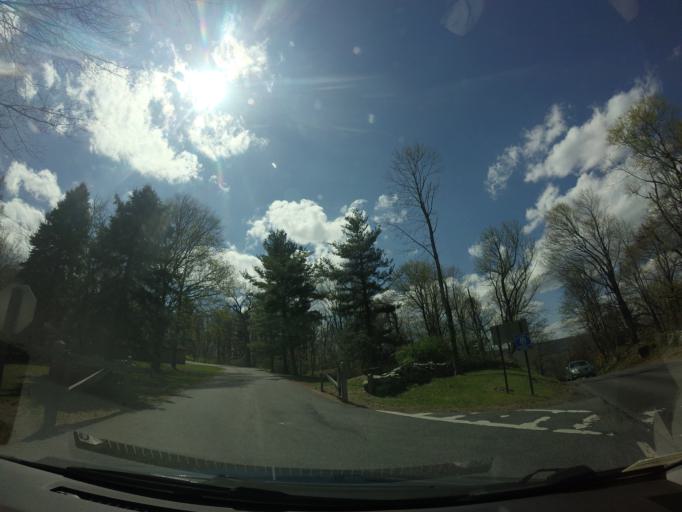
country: US
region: Maryland
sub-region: Frederick County
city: Brunswick
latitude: 39.4057
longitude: -77.6398
